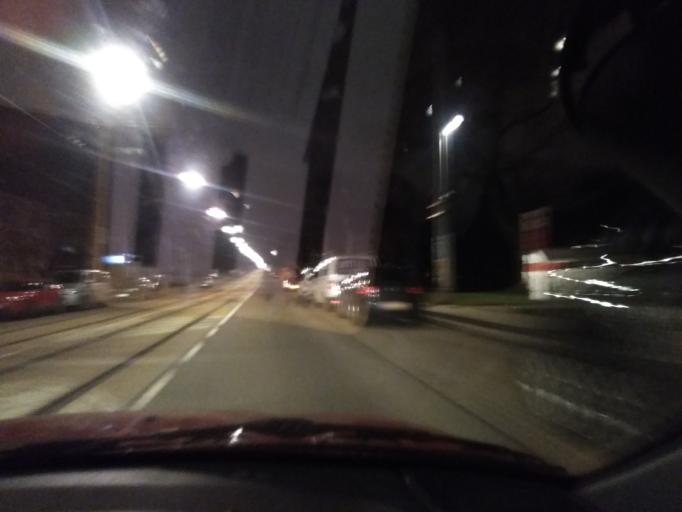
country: AT
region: Lower Austria
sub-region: Politischer Bezirk Modling
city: Perchtoldsdorf
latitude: 48.1563
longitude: 16.2735
